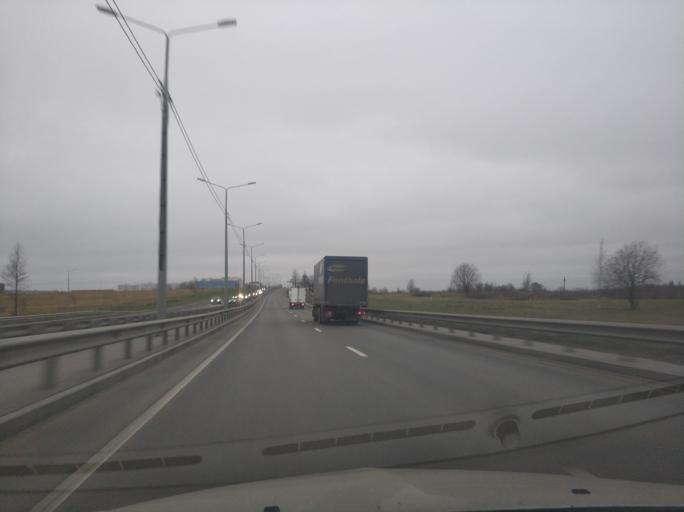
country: RU
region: St.-Petersburg
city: Pushkin
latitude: 59.7568
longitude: 30.3802
